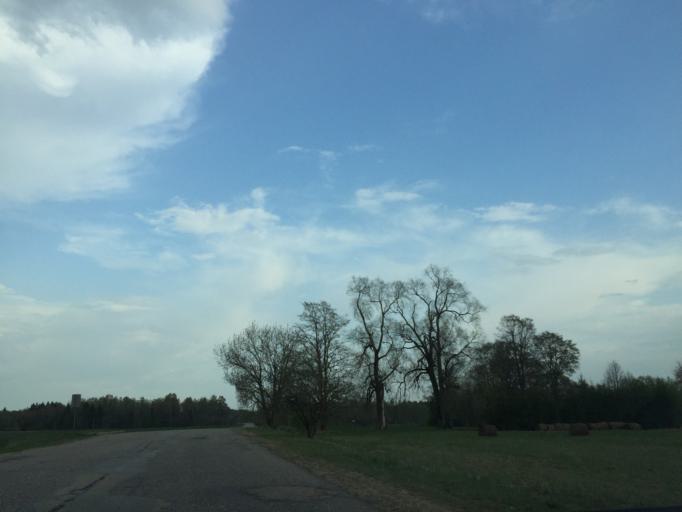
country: LV
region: Malpils
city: Malpils
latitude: 57.0139
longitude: 24.8904
